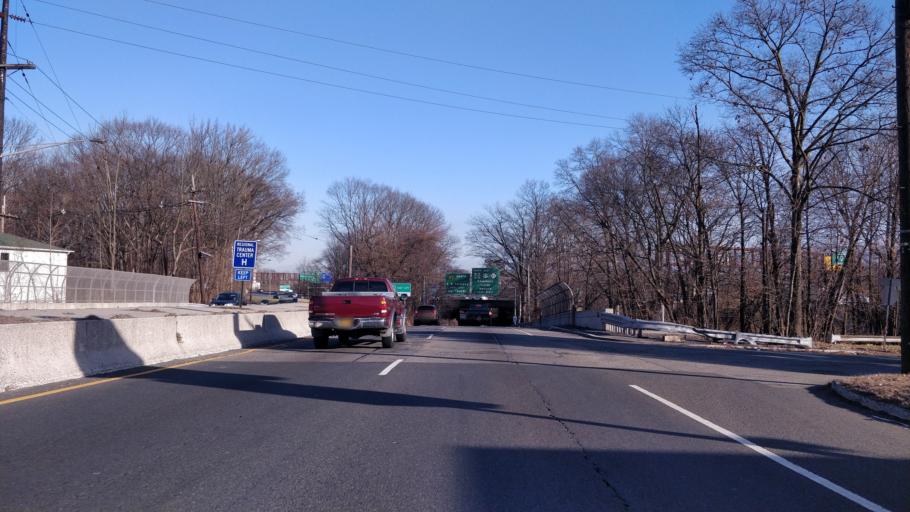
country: US
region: New Jersey
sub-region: Union County
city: Union
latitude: 40.6919
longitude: -74.2687
